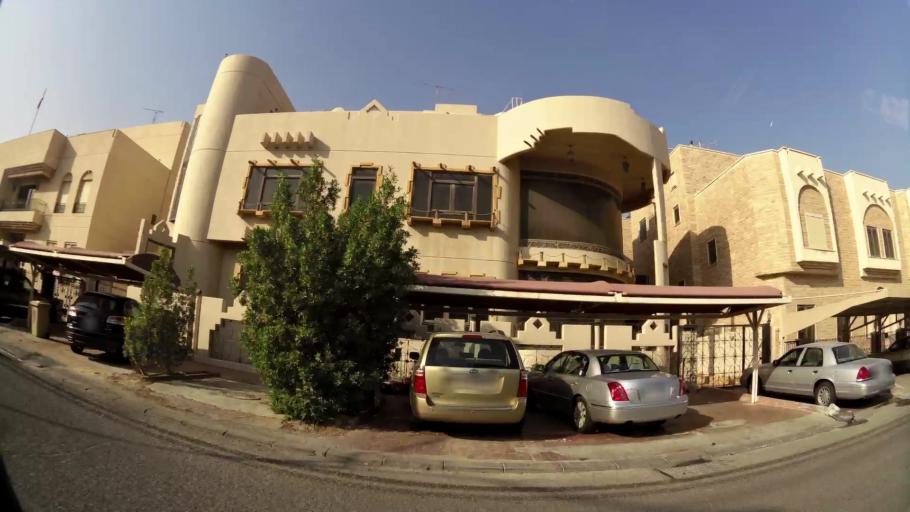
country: KW
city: Bayan
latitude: 29.3159
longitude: 48.0391
